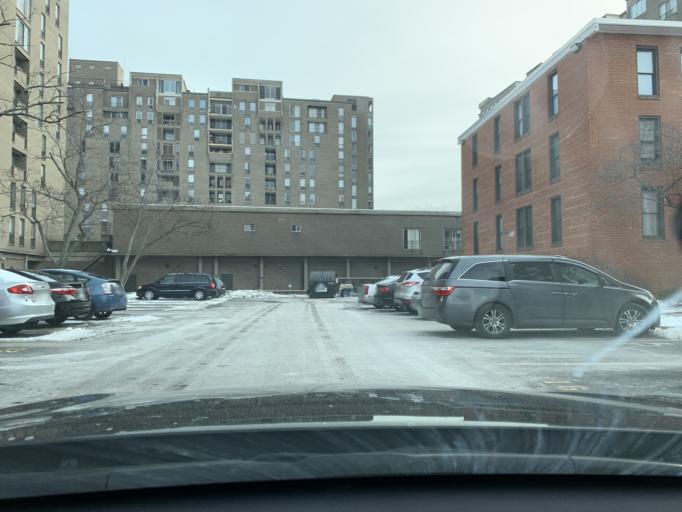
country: US
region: Massachusetts
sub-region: Norfolk County
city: Brookline
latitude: 42.3311
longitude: -71.1159
